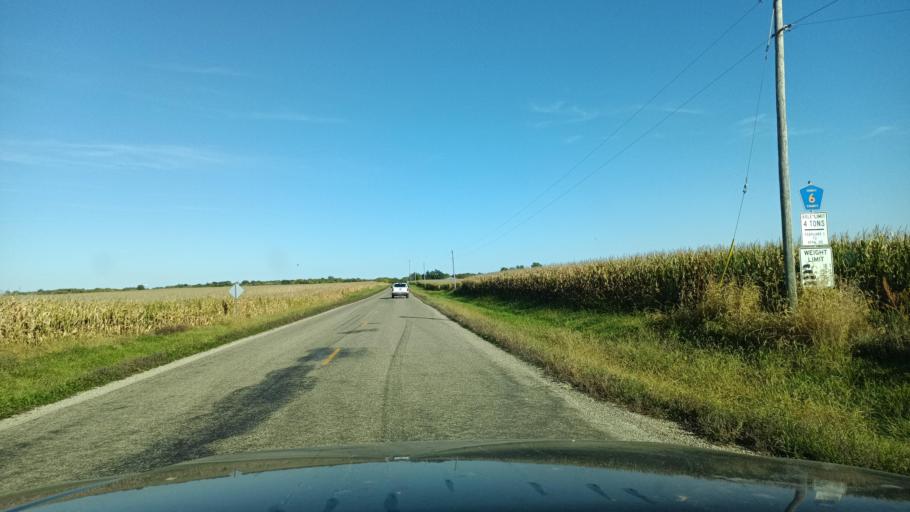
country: US
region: Illinois
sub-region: Logan County
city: Atlanta
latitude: 40.2343
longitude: -89.1478
